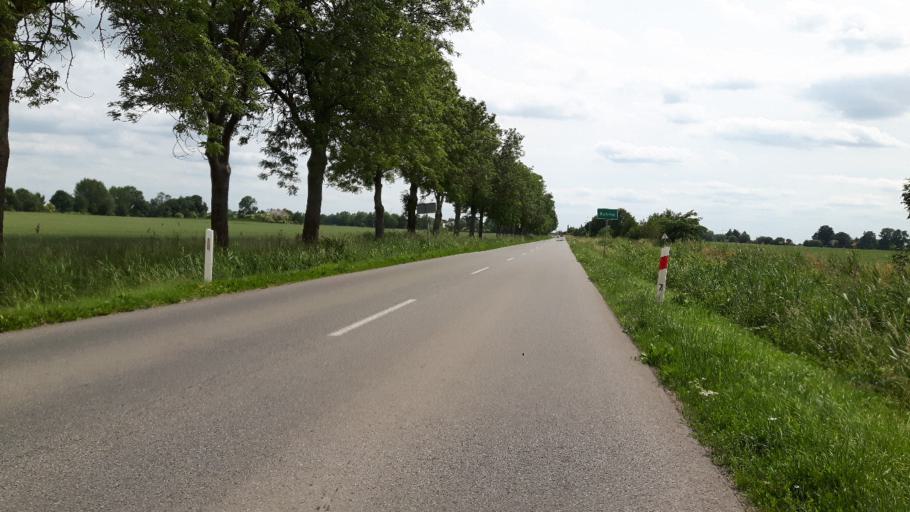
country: PL
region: Pomeranian Voivodeship
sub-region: Powiat nowodworski
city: Stegna
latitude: 54.3026
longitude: 19.1090
